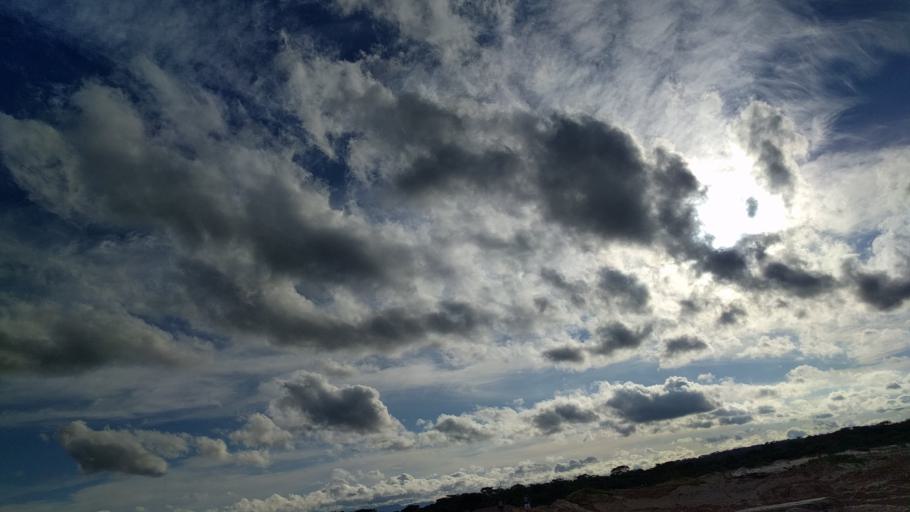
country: BO
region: Santa Cruz
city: Santa Cruz de la Sierra
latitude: -17.8529
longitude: -63.2840
